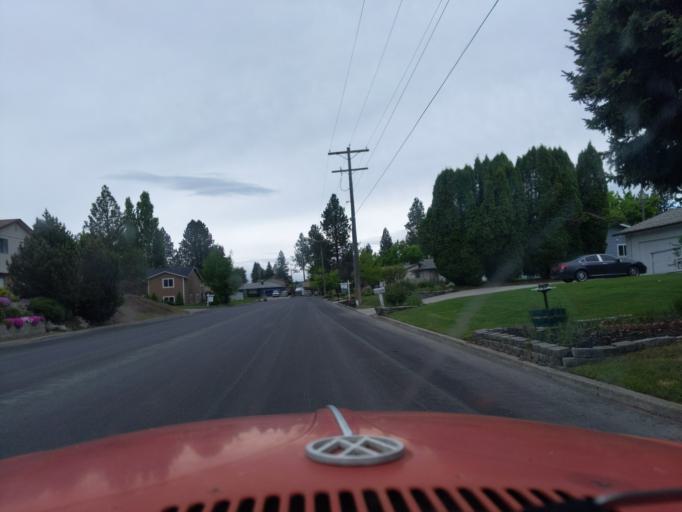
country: US
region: Washington
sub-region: Spokane County
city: Spokane
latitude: 47.5983
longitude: -117.3792
